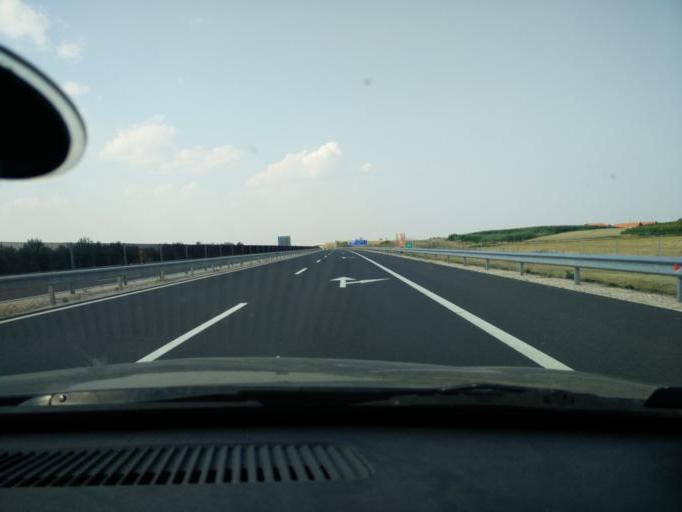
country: HU
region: Tolna
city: Dunaszentgyorgy
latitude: 46.5110
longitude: 18.7740
